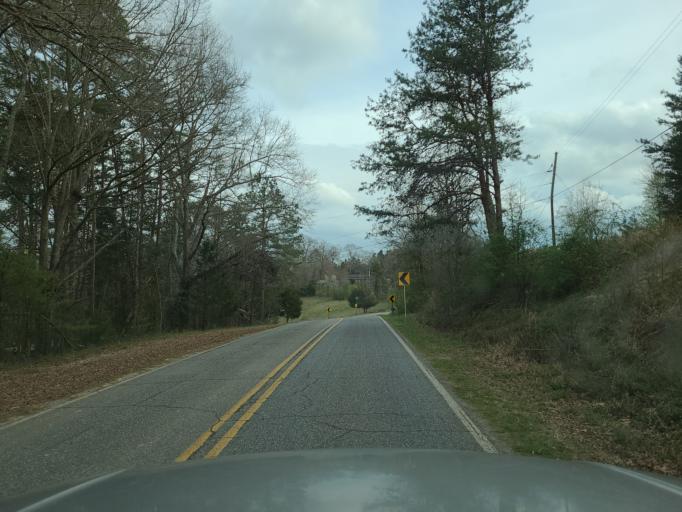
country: US
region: North Carolina
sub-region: Cleveland County
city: Boiling Springs
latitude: 35.2292
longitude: -81.7349
